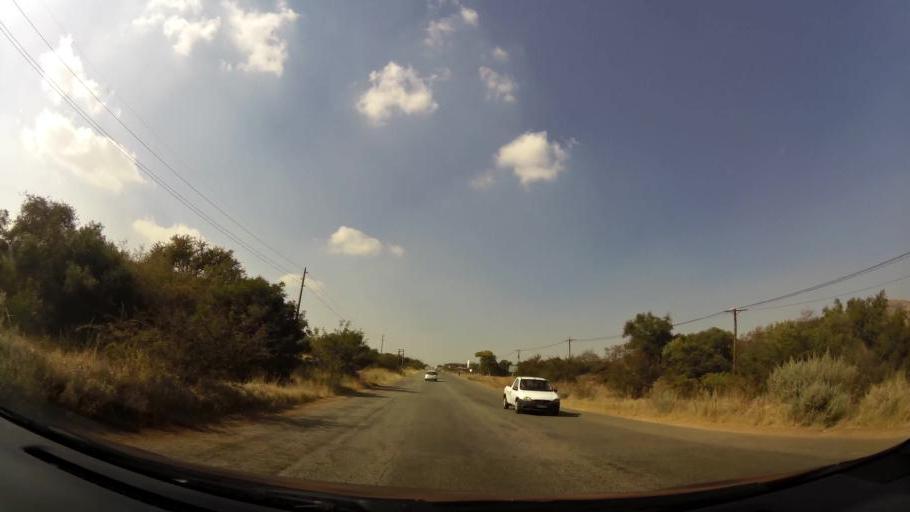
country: ZA
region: North-West
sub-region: Bojanala Platinum District Municipality
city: Rustenburg
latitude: -25.6329
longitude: 27.1725
